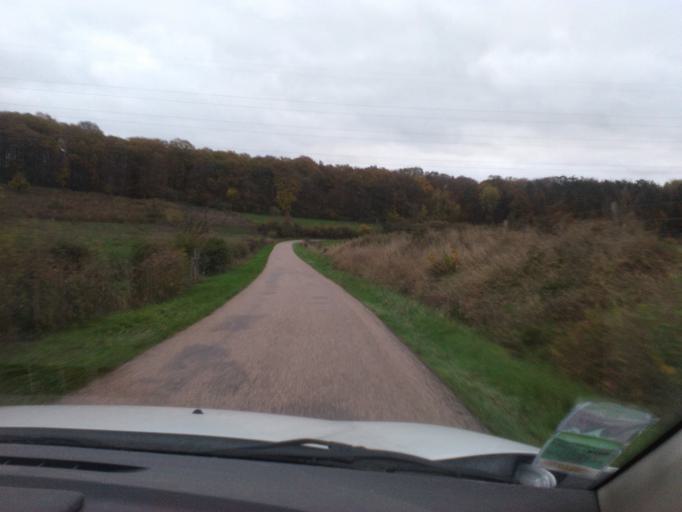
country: FR
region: Lorraine
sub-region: Departement des Vosges
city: Mirecourt
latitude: 48.3033
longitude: 6.2137
